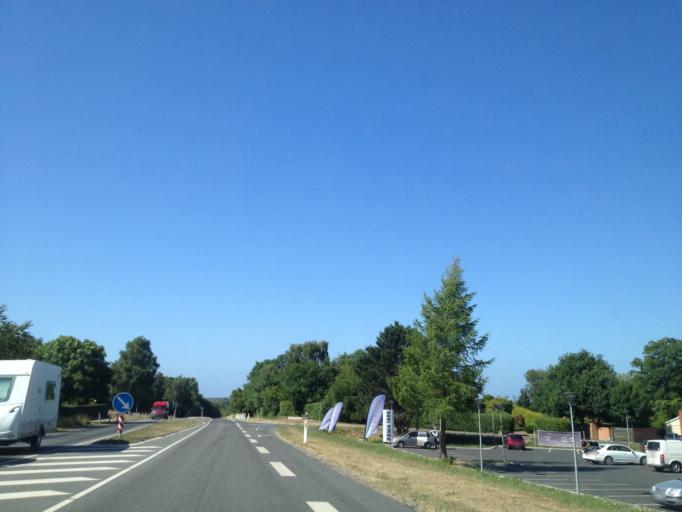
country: DK
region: Capital Region
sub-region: Gribskov Kommune
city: Graested
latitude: 56.0510
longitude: 12.3415
